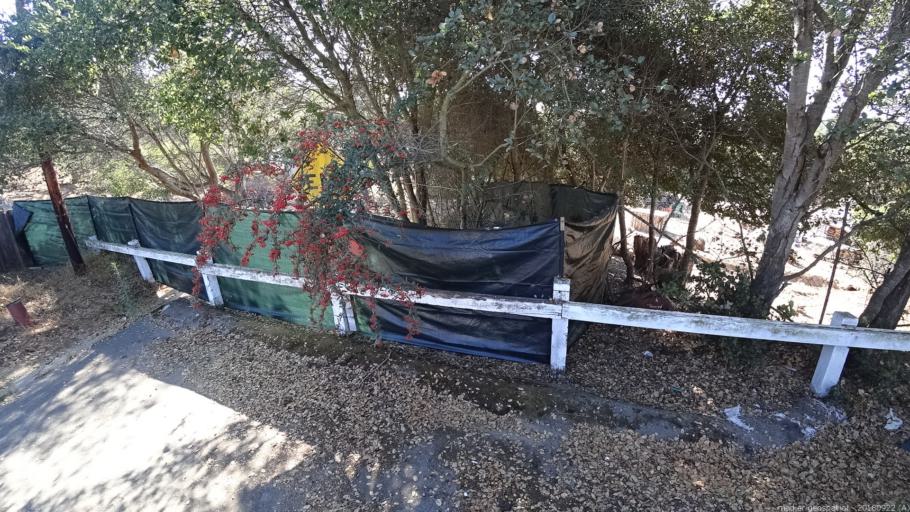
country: US
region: California
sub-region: Monterey County
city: Prunedale
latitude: 36.8193
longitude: -121.6419
